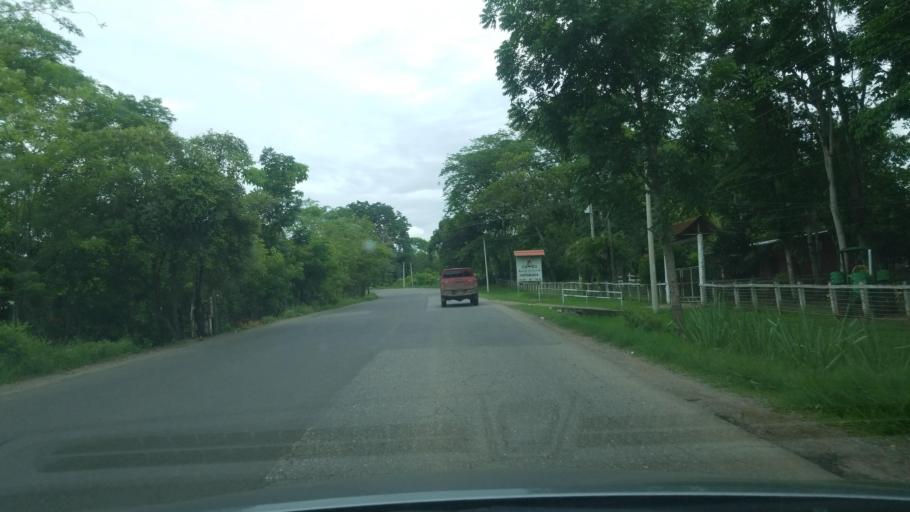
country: HN
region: Santa Barbara
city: La Flecha
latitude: 15.2989
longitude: -88.4724
